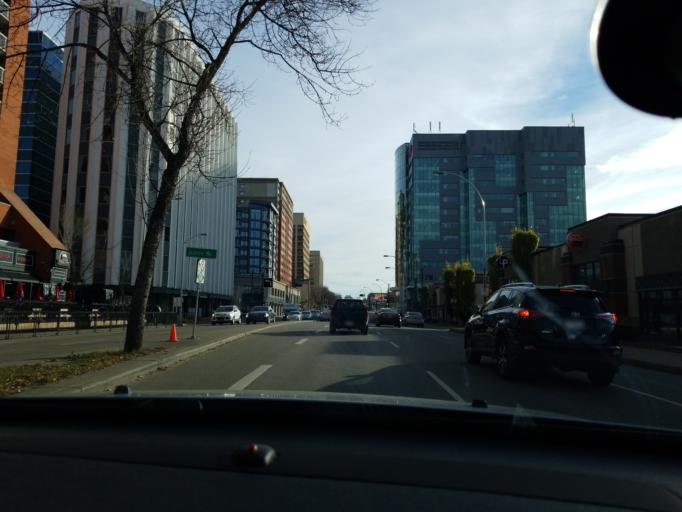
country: CA
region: Alberta
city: Edmonton
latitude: 53.5424
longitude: -113.5086
